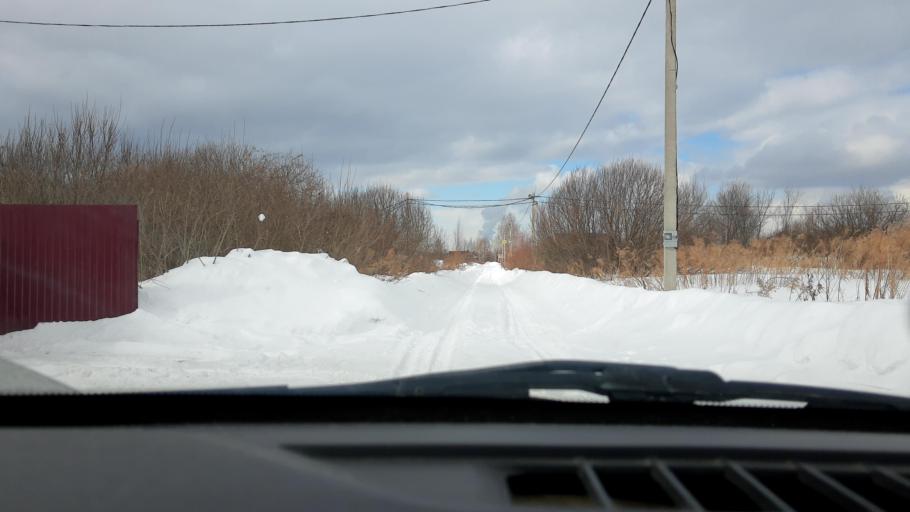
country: RU
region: Bashkortostan
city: Iglino
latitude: 54.7315
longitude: 56.2297
